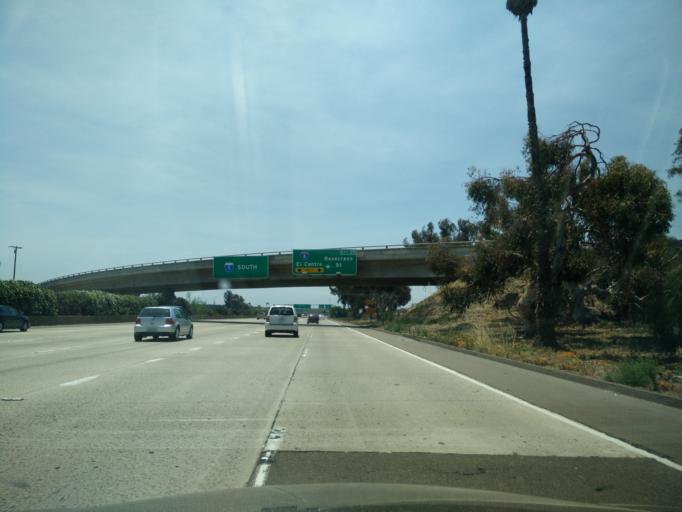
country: US
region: California
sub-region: San Diego County
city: San Diego
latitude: 32.7670
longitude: -117.2062
